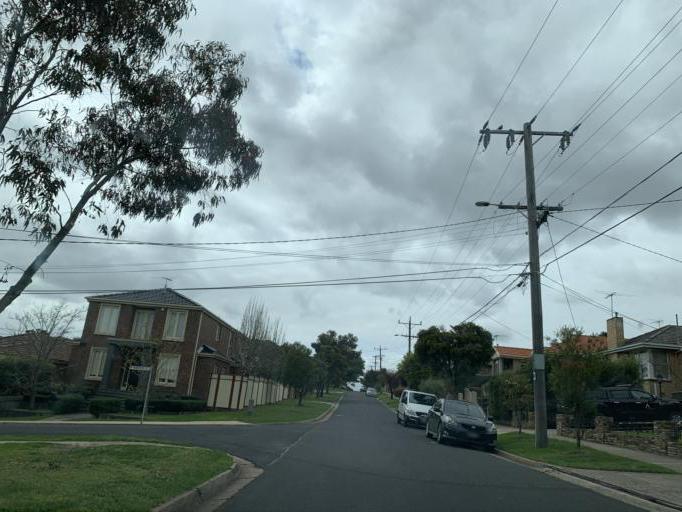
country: AU
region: Victoria
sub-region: Moreland
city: Pascoe Vale South
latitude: -37.7488
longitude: 144.9383
